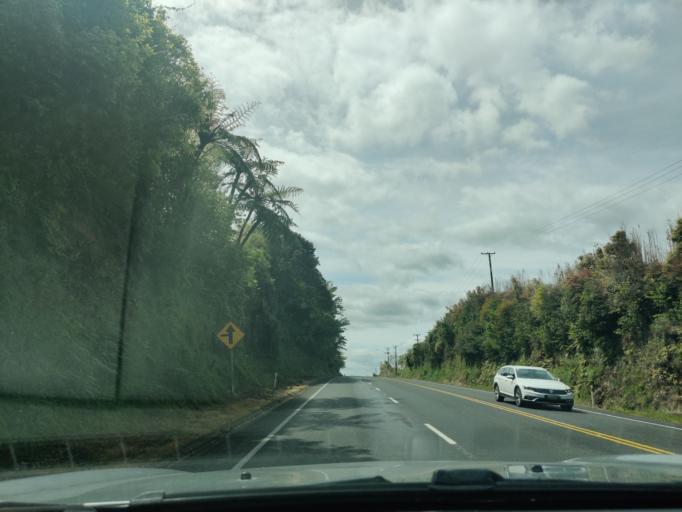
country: NZ
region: Taranaki
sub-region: New Plymouth District
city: New Plymouth
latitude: -39.1510
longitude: 174.1644
